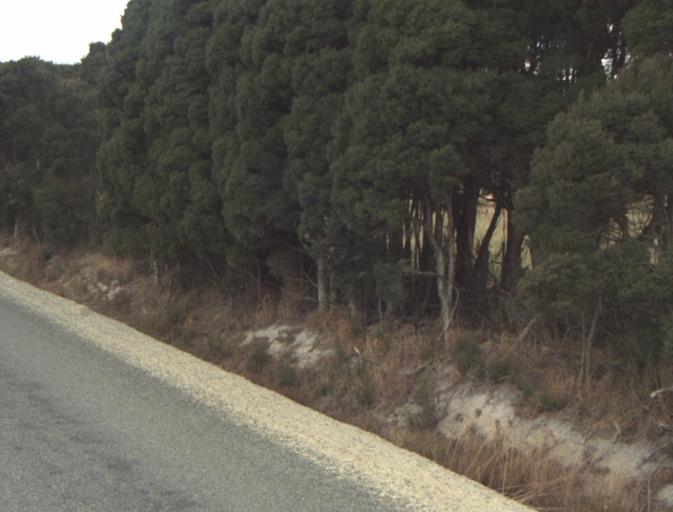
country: AU
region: Tasmania
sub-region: Launceston
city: Mayfield
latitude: -41.2046
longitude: 147.1886
